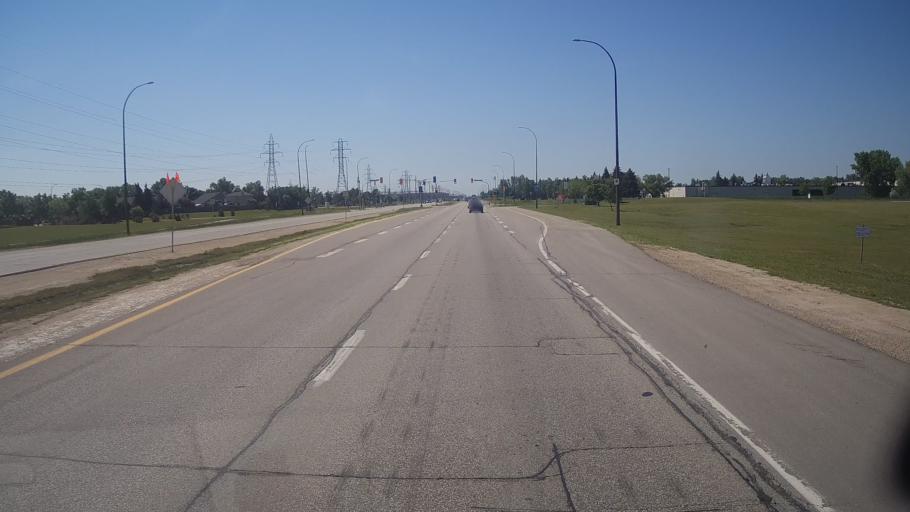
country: CA
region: Manitoba
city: Winnipeg
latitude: 49.8525
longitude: -97.0498
